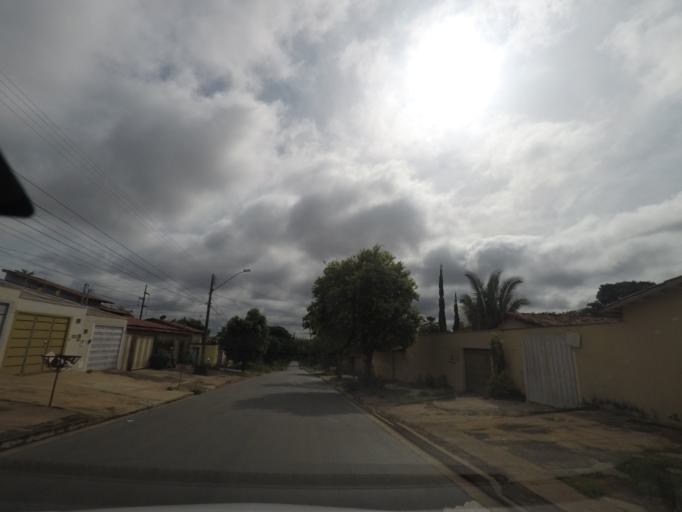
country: BR
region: Goias
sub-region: Goiania
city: Goiania
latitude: -16.7411
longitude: -49.3242
